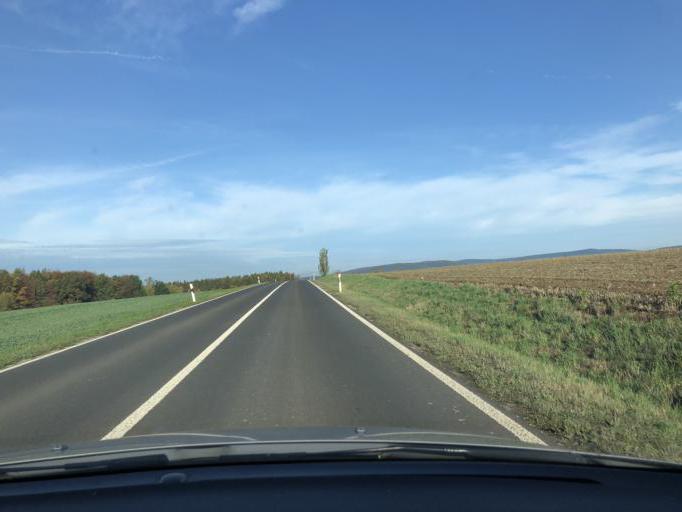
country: DE
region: Thuringia
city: Ehrenberg
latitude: 50.4721
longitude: 10.6565
